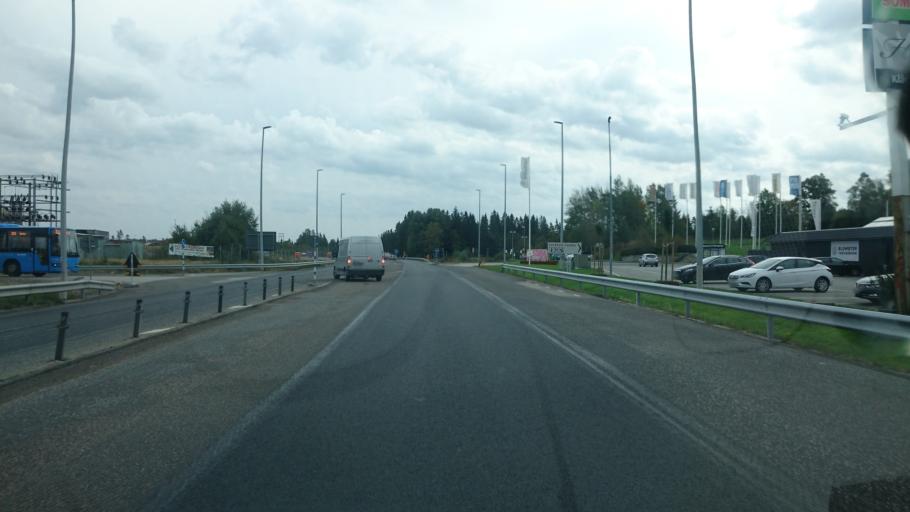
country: SE
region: Vaestra Goetaland
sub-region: Boras Kommun
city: Dalsjofors
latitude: 57.6162
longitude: 13.1126
